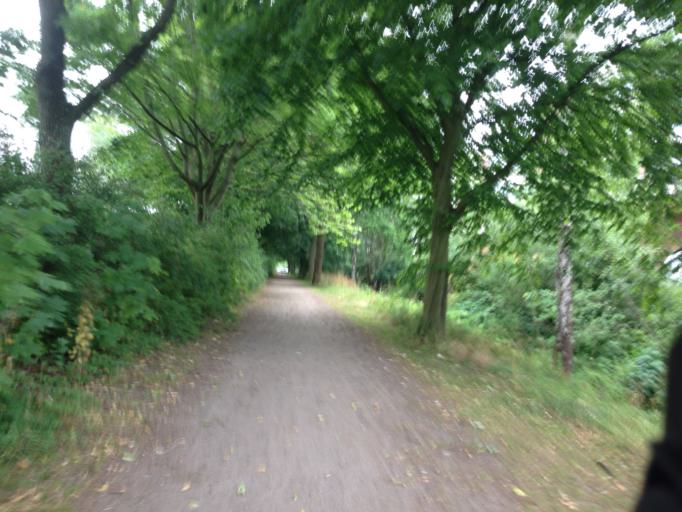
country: DE
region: Hamburg
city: Wandsbek
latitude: 53.5805
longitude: 10.1209
